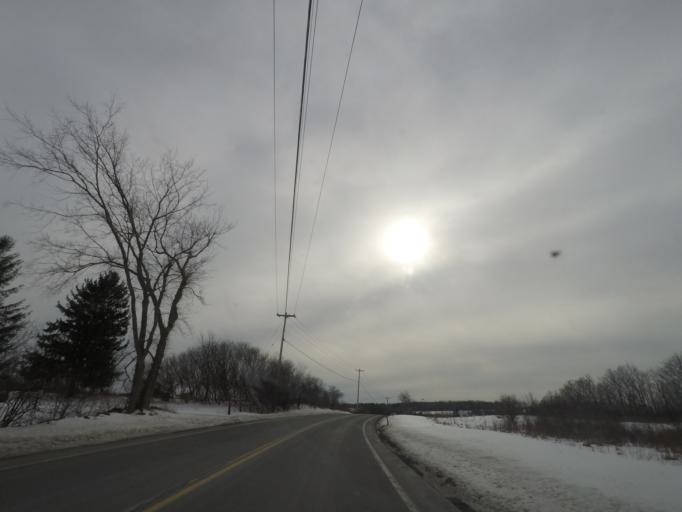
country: US
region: New York
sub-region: Albany County
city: Altamont
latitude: 42.6802
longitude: -74.0748
